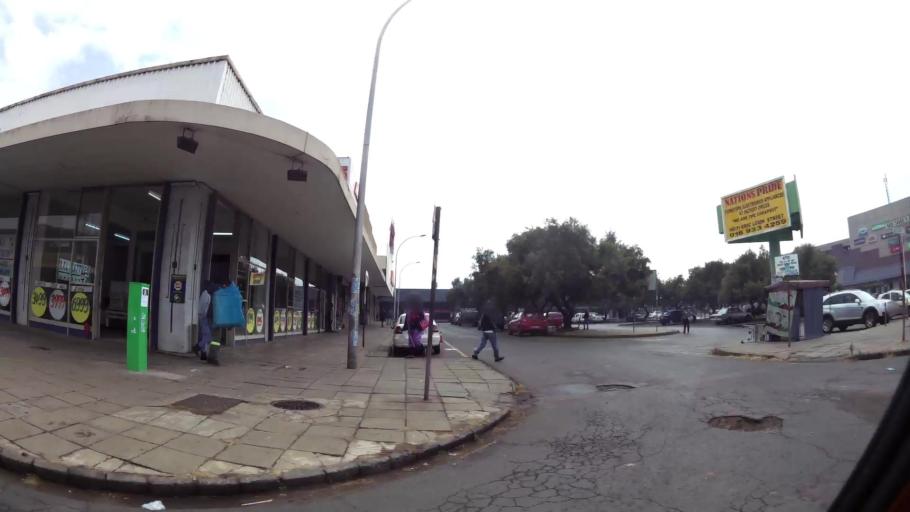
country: ZA
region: Gauteng
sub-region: Sedibeng District Municipality
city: Vanderbijlpark
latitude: -26.6990
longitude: 27.8369
